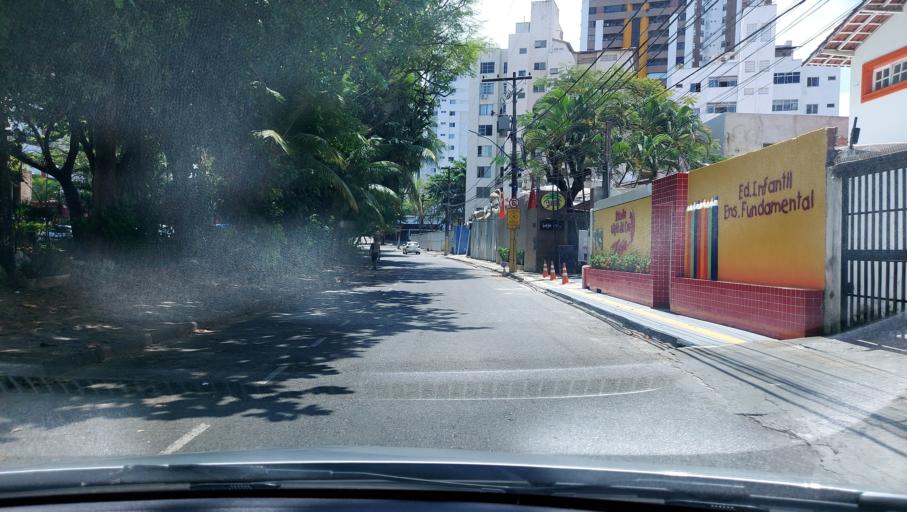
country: BR
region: Bahia
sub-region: Salvador
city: Salvador
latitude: -12.9915
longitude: -38.4534
